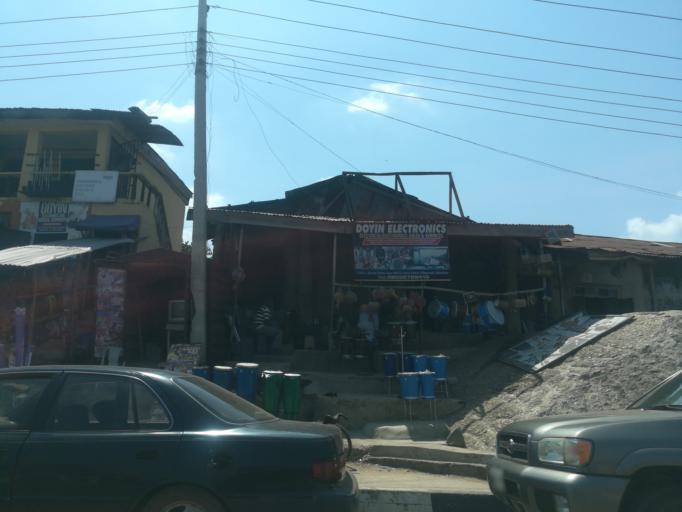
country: NG
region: Ogun
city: Abeokuta
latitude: 7.1561
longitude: 3.3438
